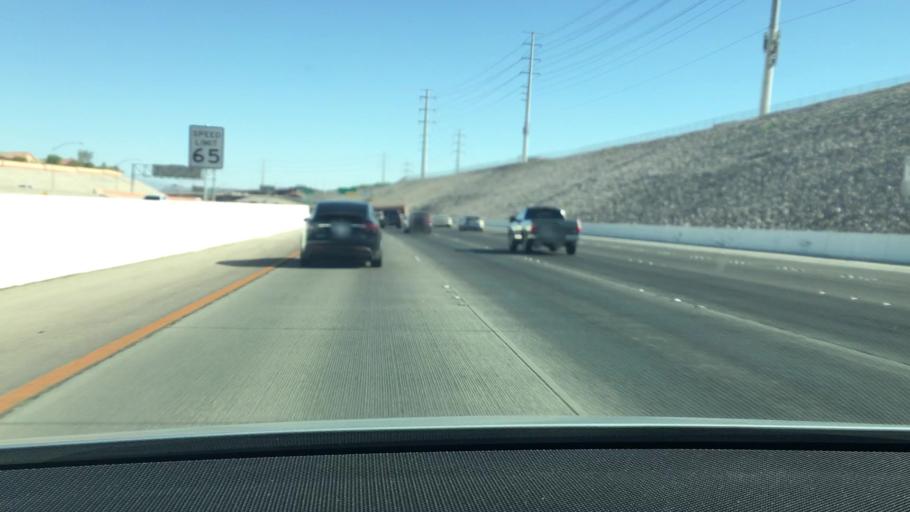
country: US
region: Nevada
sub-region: Clark County
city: Summerlin South
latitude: 36.1888
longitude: -115.3429
